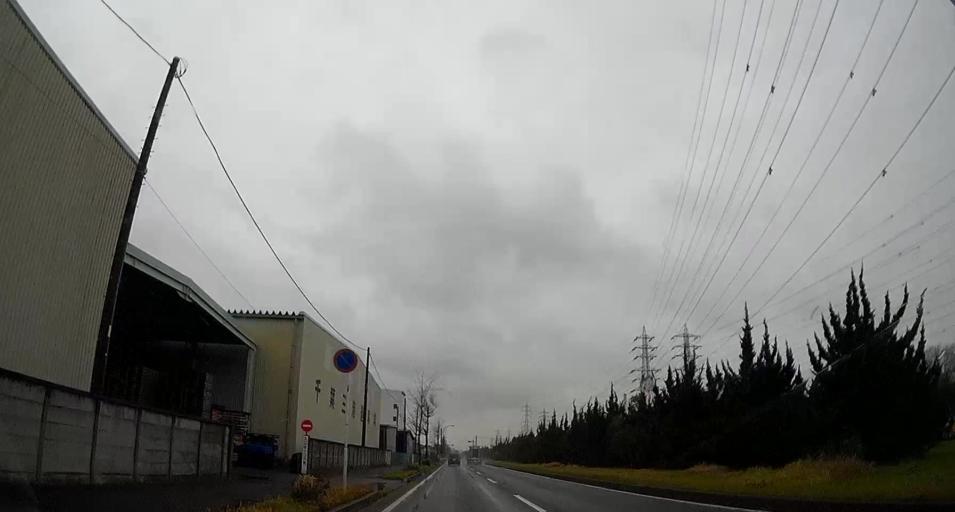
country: JP
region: Chiba
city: Ichihara
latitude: 35.4956
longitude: 140.0463
